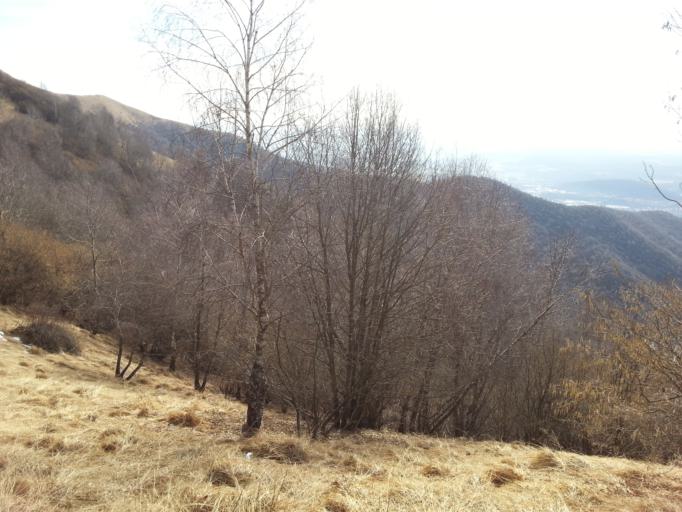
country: IT
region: Lombardy
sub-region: Provincia di Como
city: Torno
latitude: 45.8361
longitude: 9.1300
